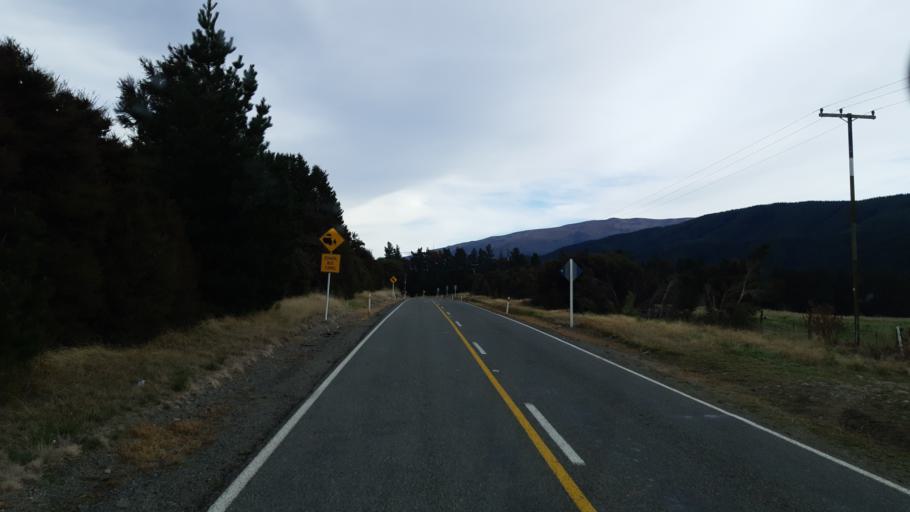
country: NZ
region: Tasman
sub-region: Tasman District
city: Brightwater
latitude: -41.6669
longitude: 173.1973
